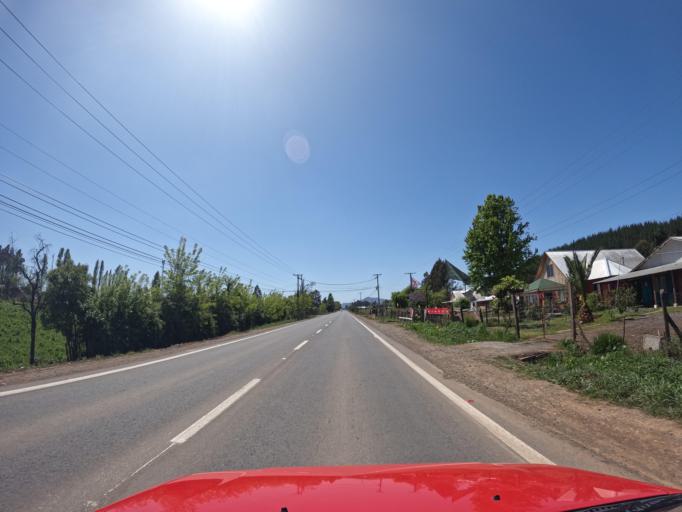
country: CL
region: Maule
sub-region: Provincia de Linares
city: Colbun
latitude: -35.7308
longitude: -71.4201
